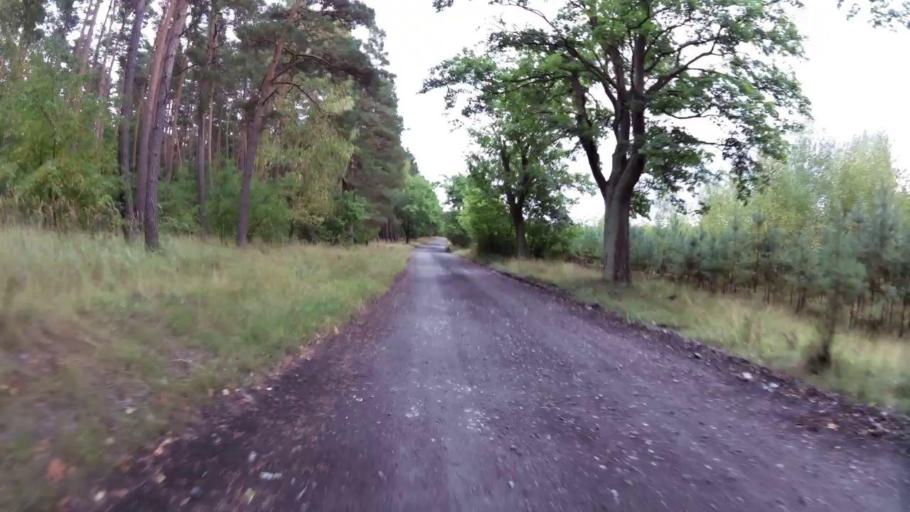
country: PL
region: West Pomeranian Voivodeship
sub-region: Powiat mysliborski
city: Debno
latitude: 52.8628
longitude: 14.7169
